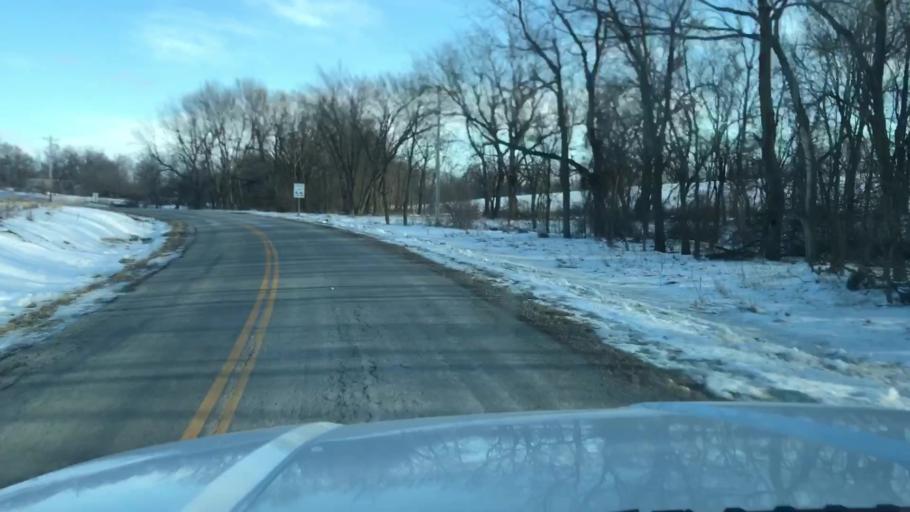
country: US
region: Missouri
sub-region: Holt County
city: Oregon
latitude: 40.1013
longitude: -95.0210
